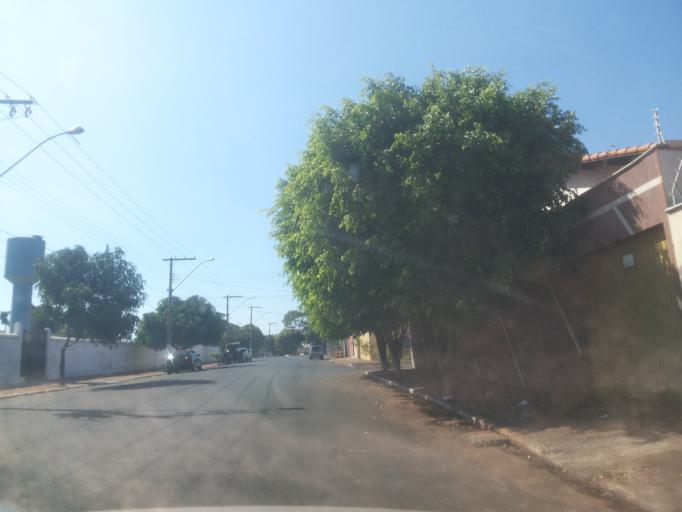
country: BR
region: Minas Gerais
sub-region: Ituiutaba
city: Ituiutaba
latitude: -18.9673
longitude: -49.4535
